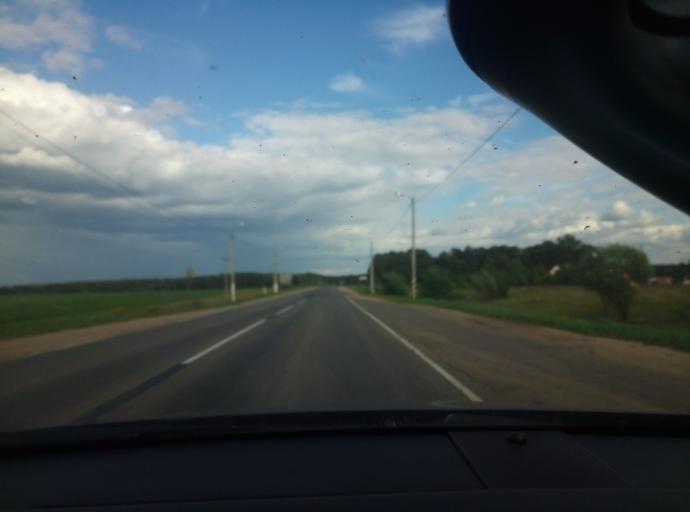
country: RU
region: Kaluga
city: Nikola-Lenivets
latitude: 54.5632
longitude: 35.4782
